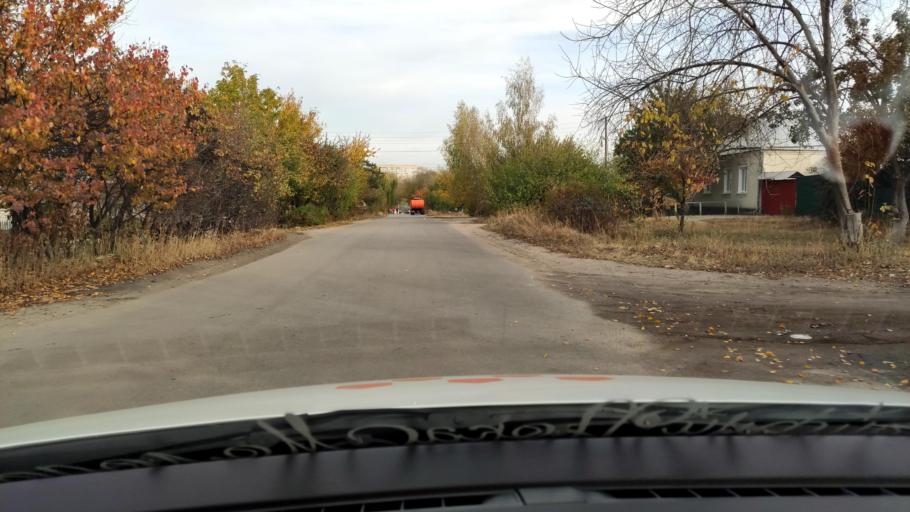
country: RU
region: Voronezj
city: Voronezh
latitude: 51.6810
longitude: 39.1367
